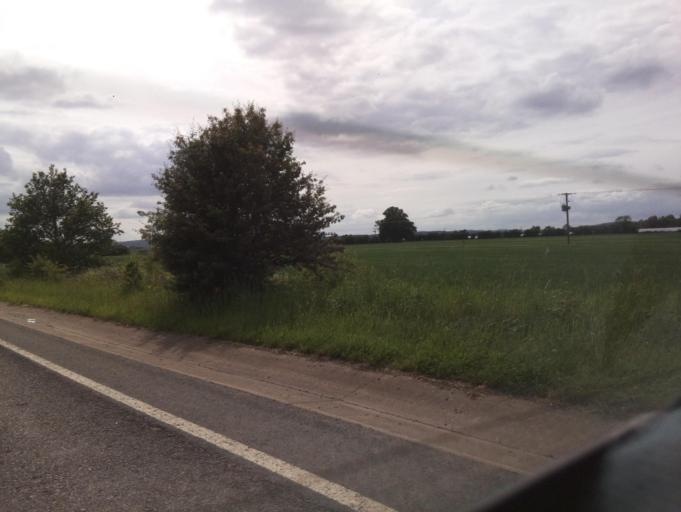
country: GB
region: England
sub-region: Worcestershire
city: Bransford
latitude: 52.1814
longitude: -2.2767
